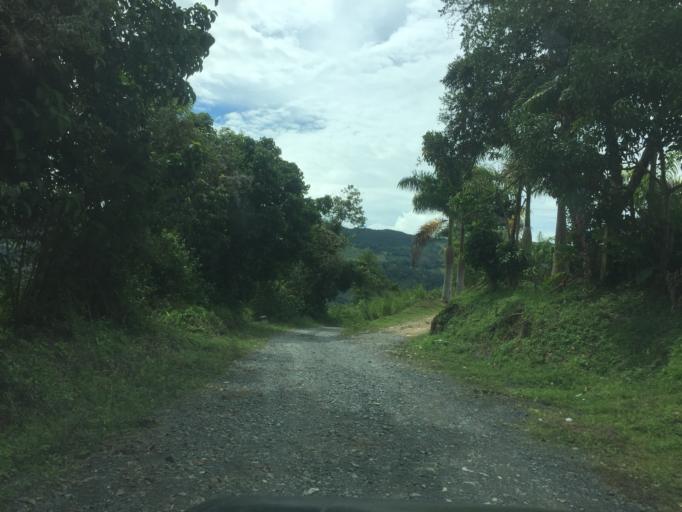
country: CO
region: Santander
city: Guepsa
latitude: 6.0218
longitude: -73.5499
